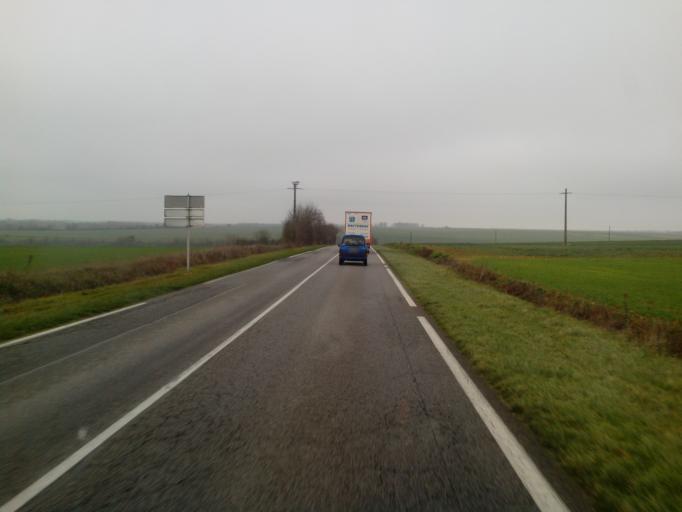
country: FR
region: Poitou-Charentes
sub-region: Departement de la Vienne
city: Vouille
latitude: 46.6525
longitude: 0.1252
